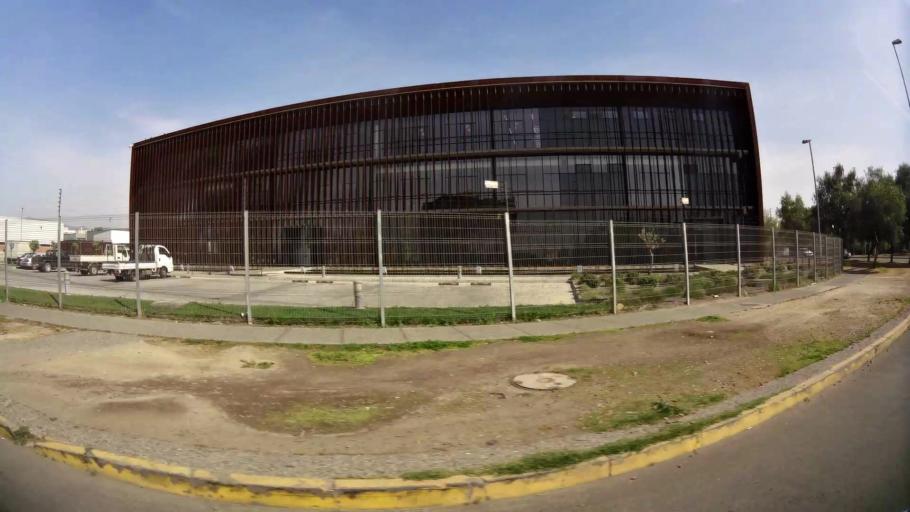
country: CL
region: Santiago Metropolitan
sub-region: Provincia de Santiago
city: Lo Prado
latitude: -33.4281
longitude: -70.7786
